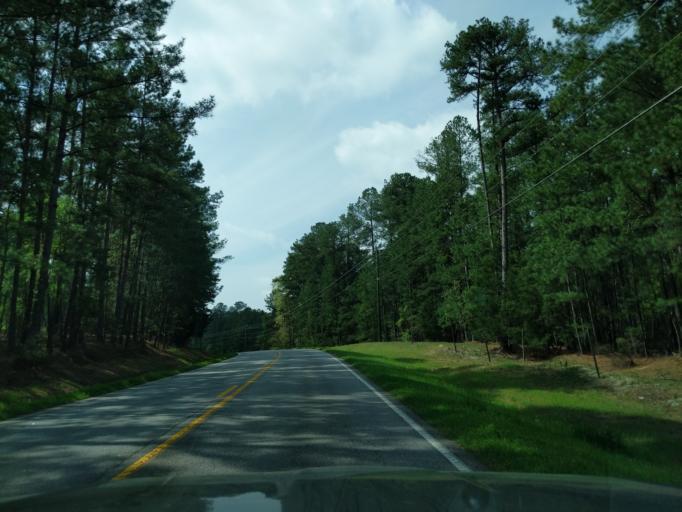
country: US
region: Georgia
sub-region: Columbia County
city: Appling
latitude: 33.5685
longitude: -82.3221
